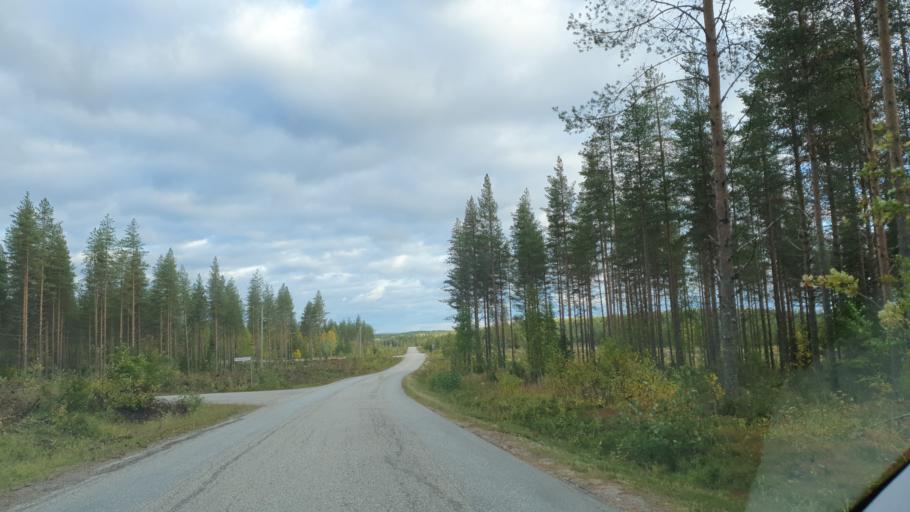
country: FI
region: North Karelia
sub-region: Pielisen Karjala
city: Lieksa
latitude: 63.9207
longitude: 30.1570
